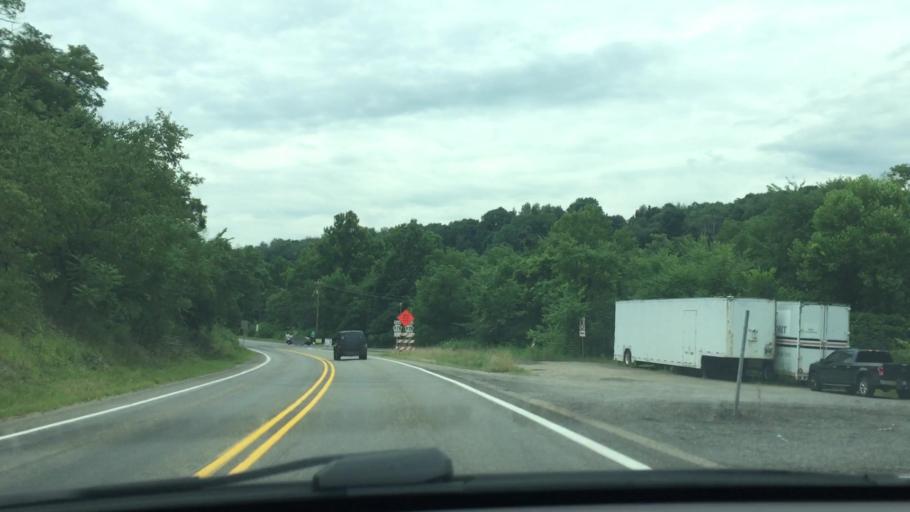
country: US
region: Pennsylvania
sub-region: Allegheny County
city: Oakdale
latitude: 40.4105
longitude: -80.1921
